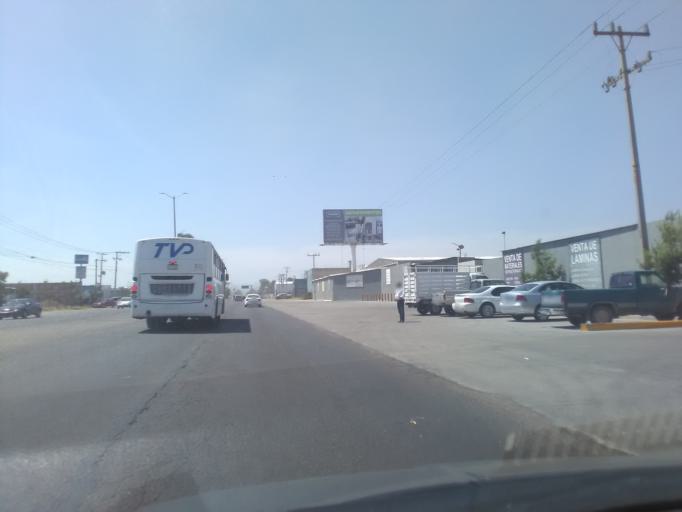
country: MX
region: Durango
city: Victoria de Durango
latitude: 24.0298
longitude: -104.6062
